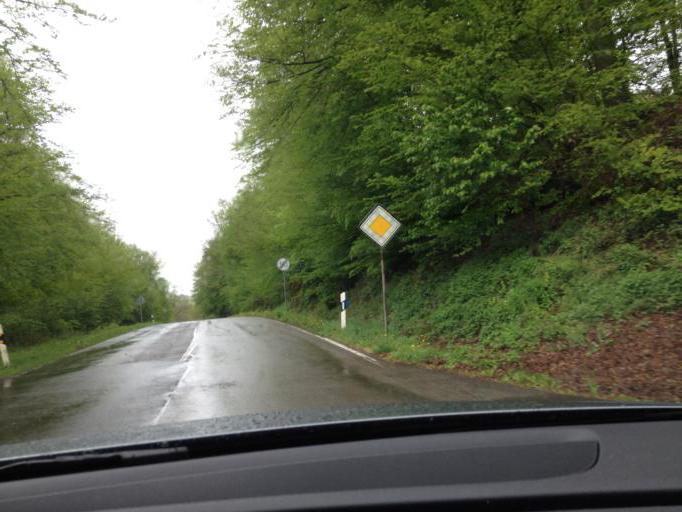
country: DE
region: Saarland
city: Freisen
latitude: 49.4931
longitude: 7.2333
